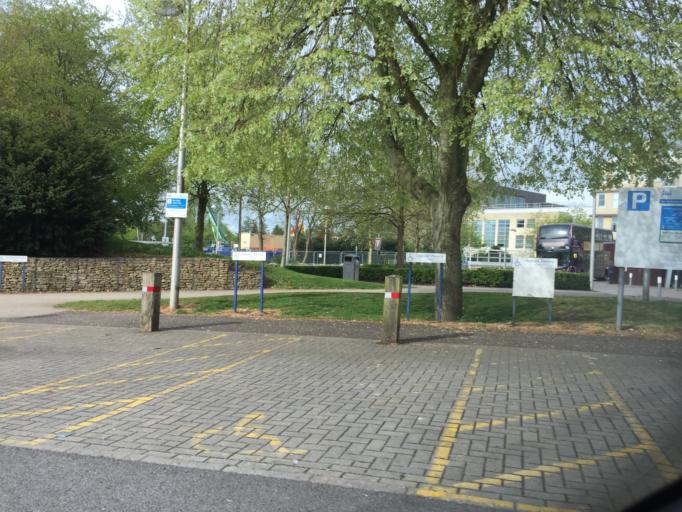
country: GB
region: England
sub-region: Bath and North East Somerset
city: Bath
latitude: 51.3792
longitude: -2.3245
